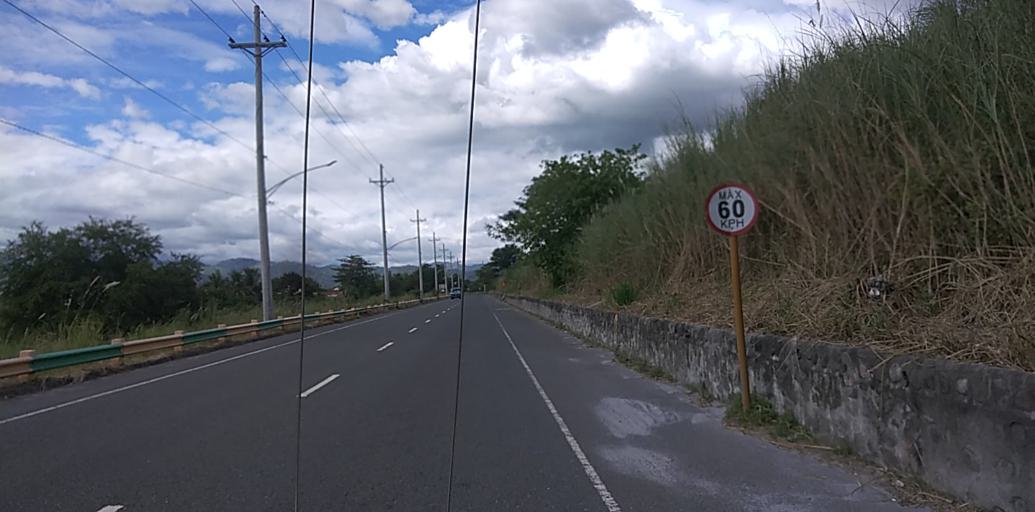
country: PH
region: Central Luzon
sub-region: Province of Pampanga
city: Dolores
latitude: 15.0967
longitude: 120.5280
